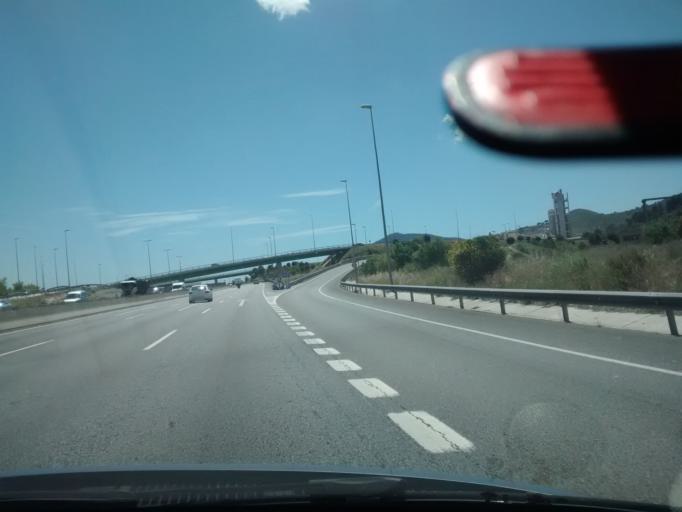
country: ES
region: Catalonia
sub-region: Provincia de Barcelona
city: Palleja
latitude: 41.4192
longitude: 2.0035
